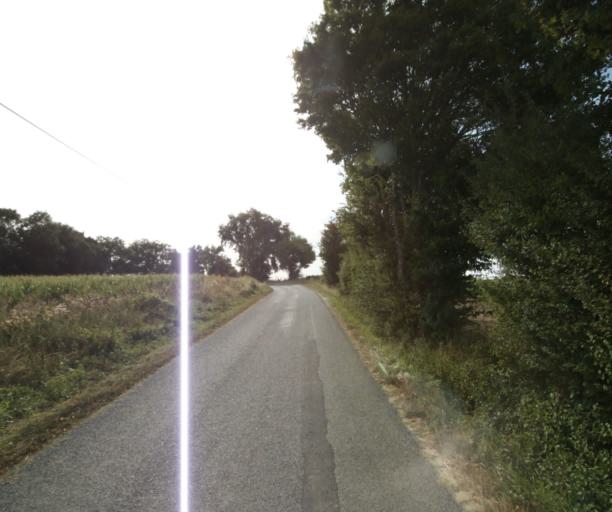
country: FR
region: Midi-Pyrenees
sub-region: Departement du Tarn
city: Puylaurens
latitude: 43.5253
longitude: 2.0353
